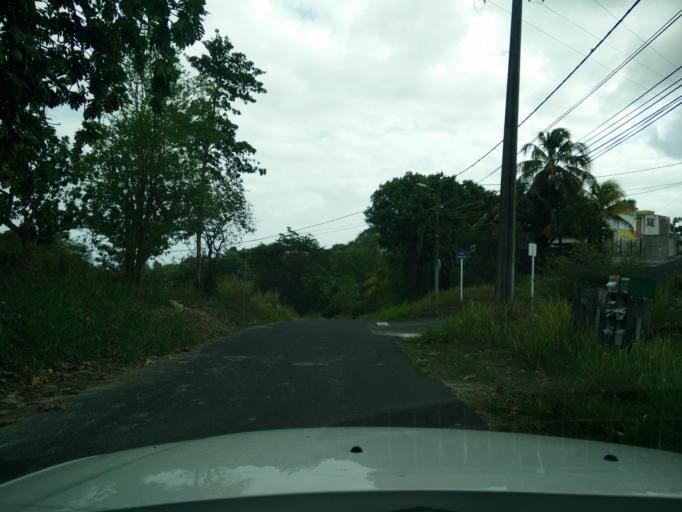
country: GP
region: Guadeloupe
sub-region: Guadeloupe
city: Le Gosier
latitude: 16.2340
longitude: -61.4414
